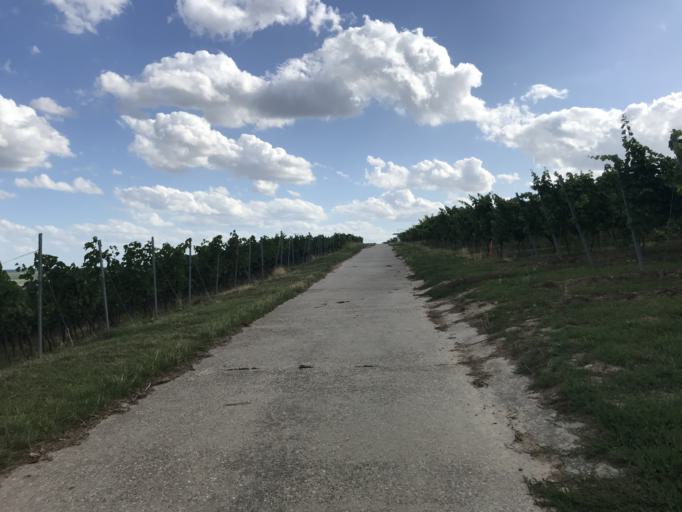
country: DE
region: Rheinland-Pfalz
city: Bodenheim
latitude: 49.9420
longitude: 8.2984
